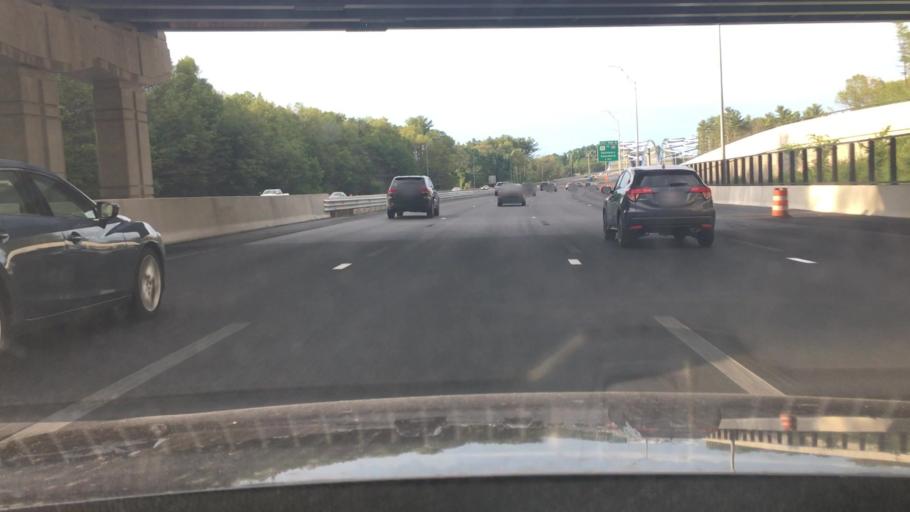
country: US
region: Massachusetts
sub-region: Essex County
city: Amesbury
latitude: 42.8292
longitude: -70.9151
